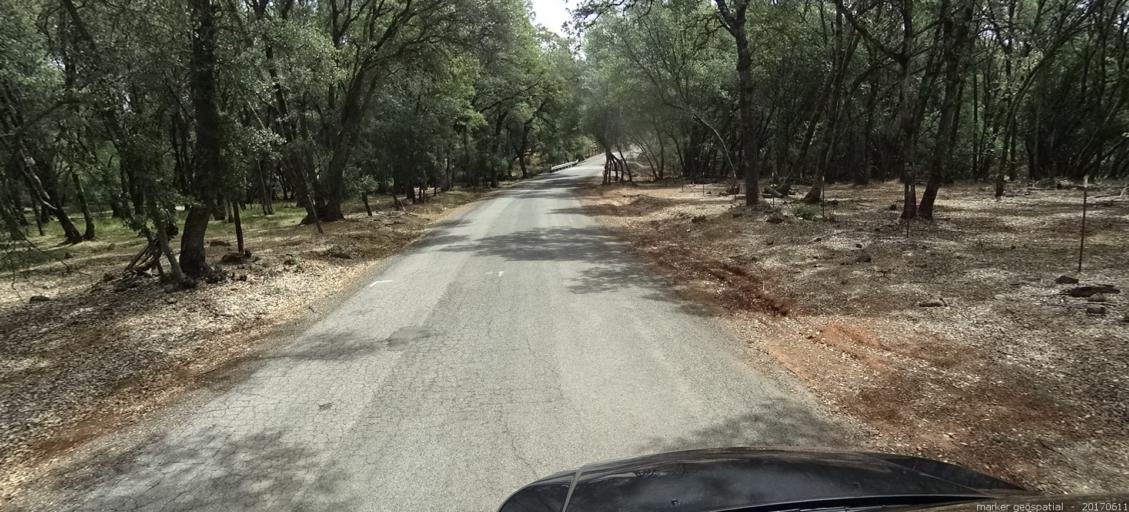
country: US
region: California
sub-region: Butte County
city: Oroville
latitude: 39.5983
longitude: -121.5356
